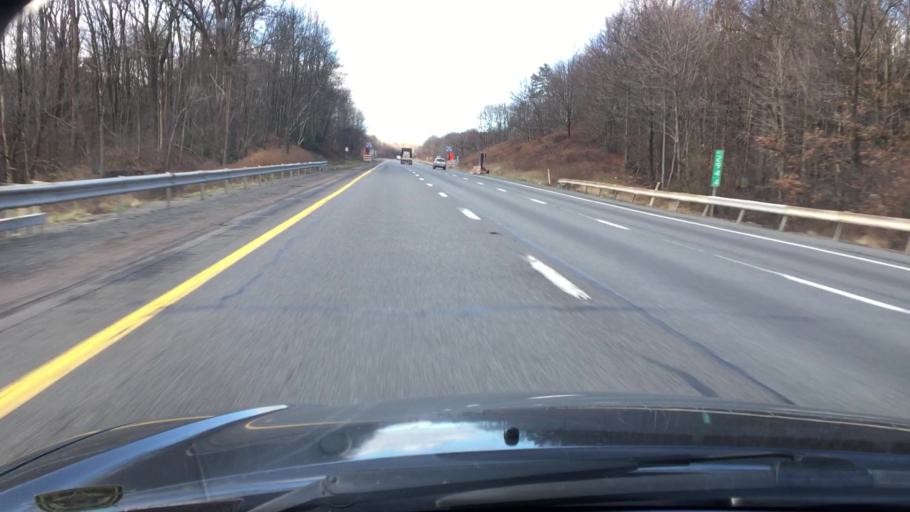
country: US
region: Pennsylvania
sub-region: Monroe County
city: Emerald Lakes
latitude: 41.0651
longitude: -75.3741
